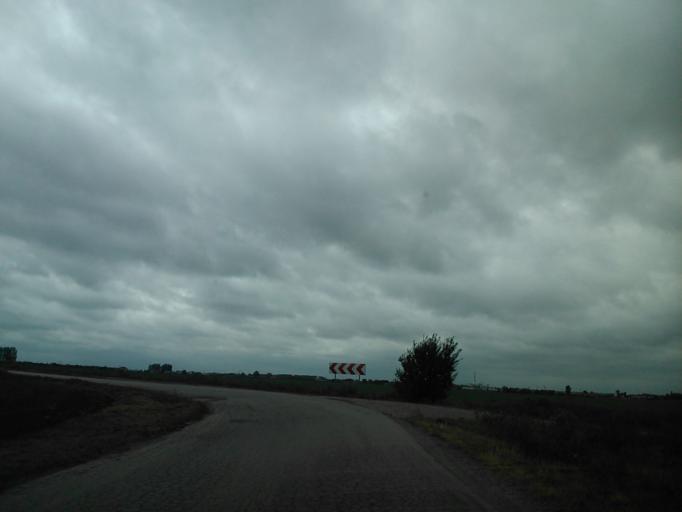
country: PL
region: Kujawsko-Pomorskie
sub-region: Powiat inowroclawski
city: Inowroclaw
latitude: 52.7608
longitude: 18.3133
